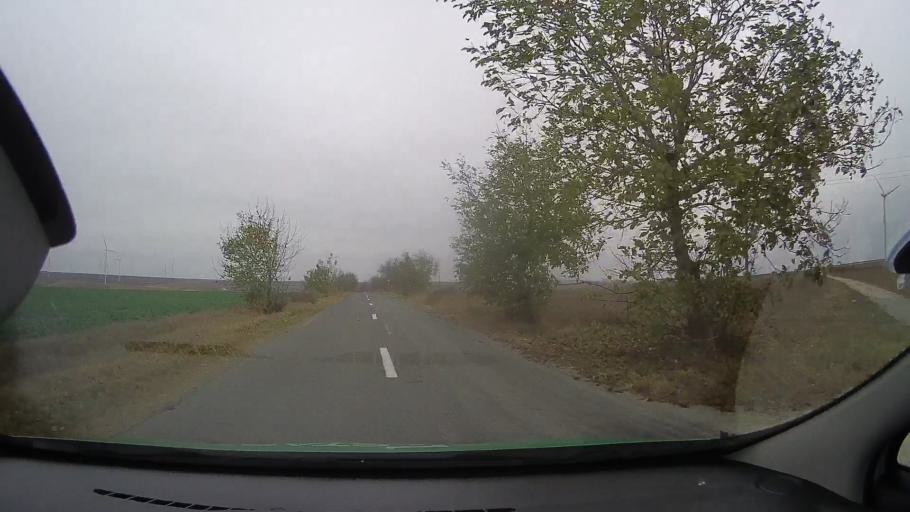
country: RO
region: Constanta
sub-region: Comuna Targusor
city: Targusor
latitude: 44.4809
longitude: 28.3728
